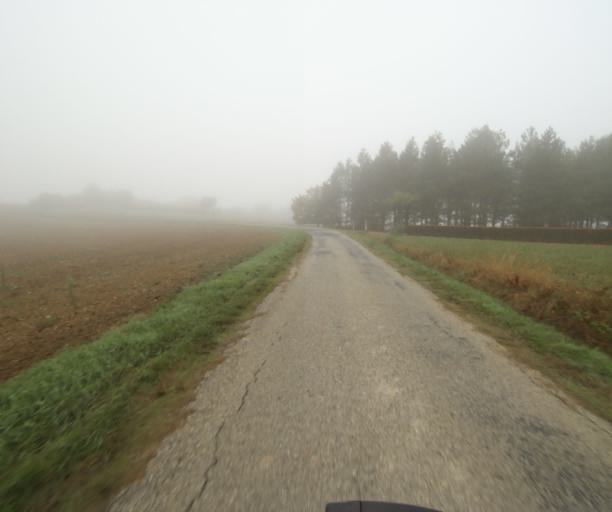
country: FR
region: Midi-Pyrenees
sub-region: Departement du Tarn-et-Garonne
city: Nohic
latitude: 43.9338
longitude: 1.4769
